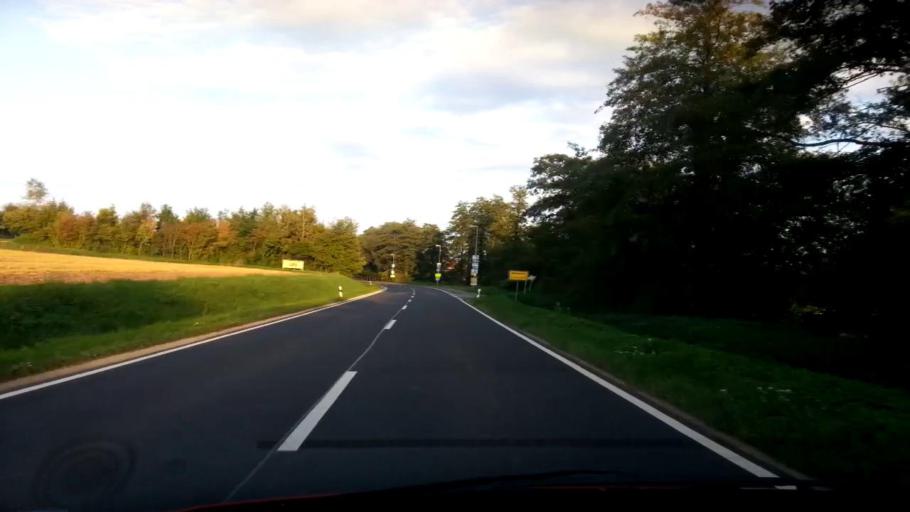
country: DE
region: Bavaria
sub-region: Upper Franconia
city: Burgwindheim
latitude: 49.8285
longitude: 10.5898
